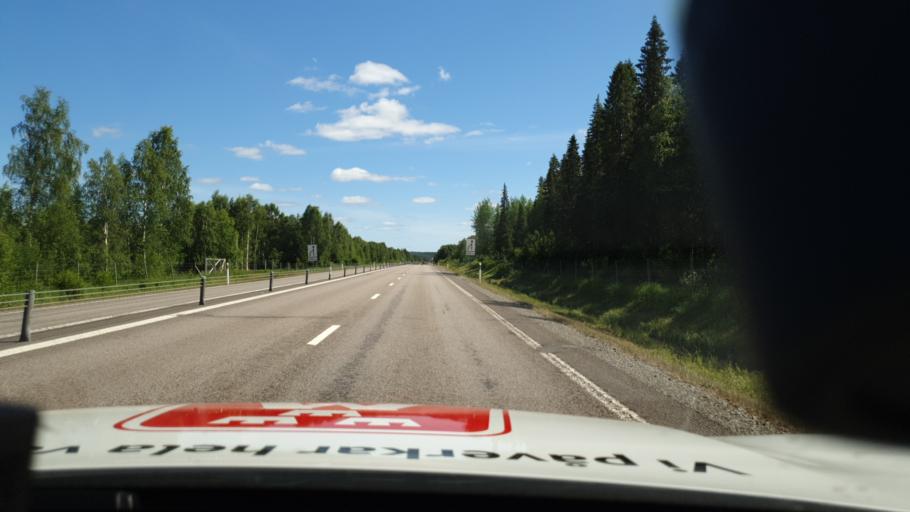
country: SE
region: Norrbotten
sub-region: Kalix Kommun
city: Toere
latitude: 65.8981
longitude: 22.8773
